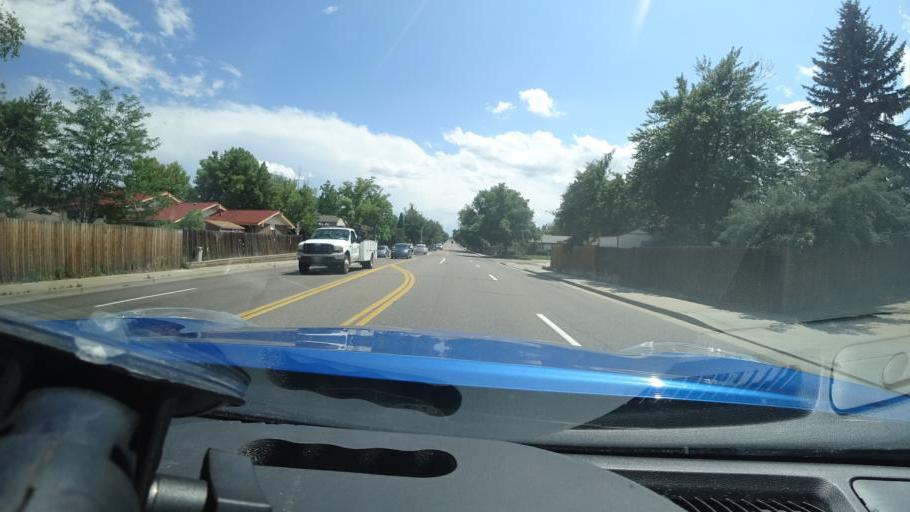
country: US
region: Colorado
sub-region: Adams County
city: Aurora
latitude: 39.6935
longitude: -104.8471
